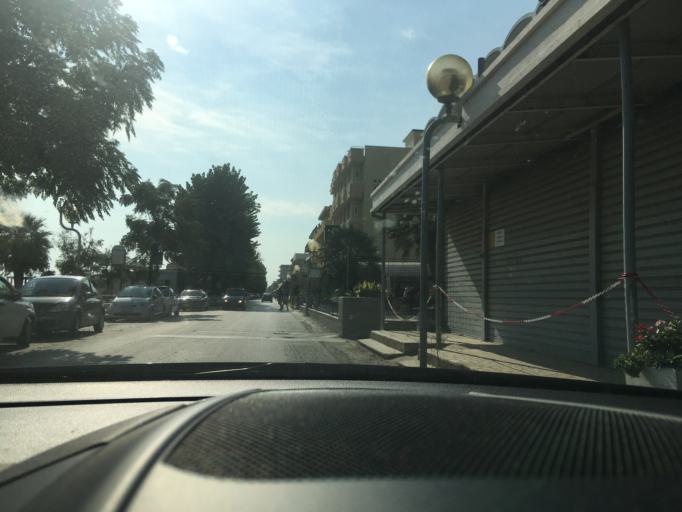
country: IT
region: Emilia-Romagna
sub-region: Provincia di Rimini
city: Santa Giustina
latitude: 44.1098
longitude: 12.5092
